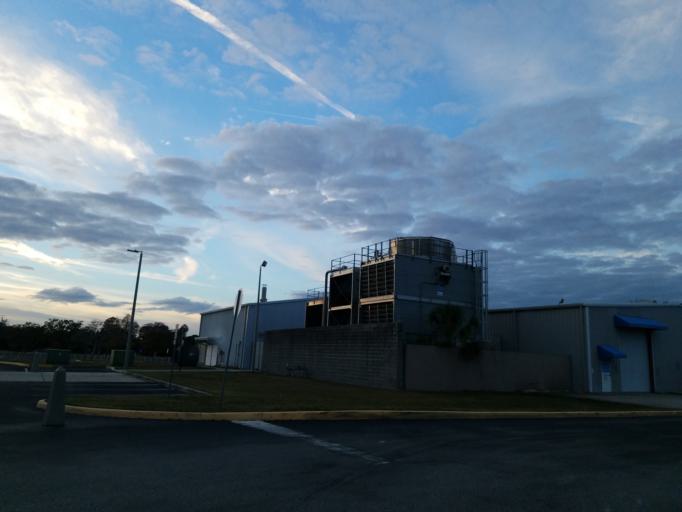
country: US
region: Florida
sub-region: Hillsborough County
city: Egypt Lake-Leto
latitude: 27.9766
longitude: -82.5095
